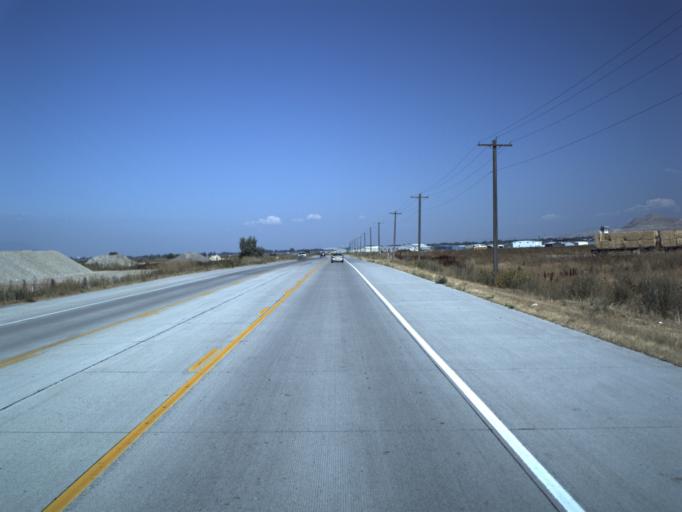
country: US
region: Utah
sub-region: Cache County
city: Logan
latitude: 41.7705
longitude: -111.8585
